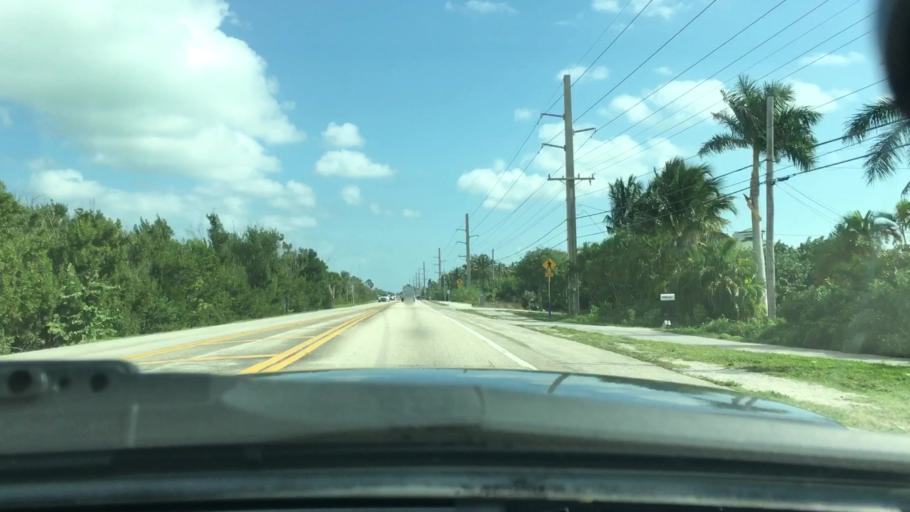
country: US
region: Florida
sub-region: Monroe County
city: Cudjoe Key
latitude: 24.6622
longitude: -81.4596
